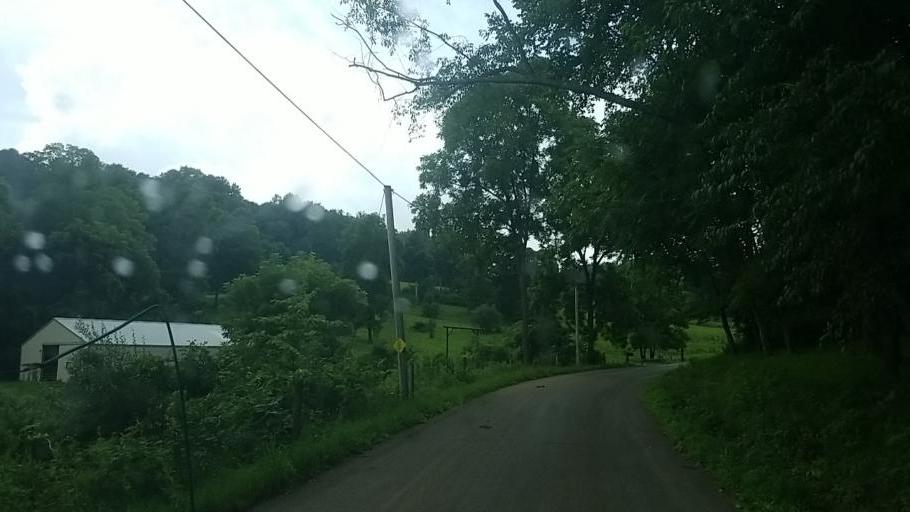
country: US
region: Ohio
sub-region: Muskingum County
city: Frazeysburg
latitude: 40.1564
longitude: -82.2669
